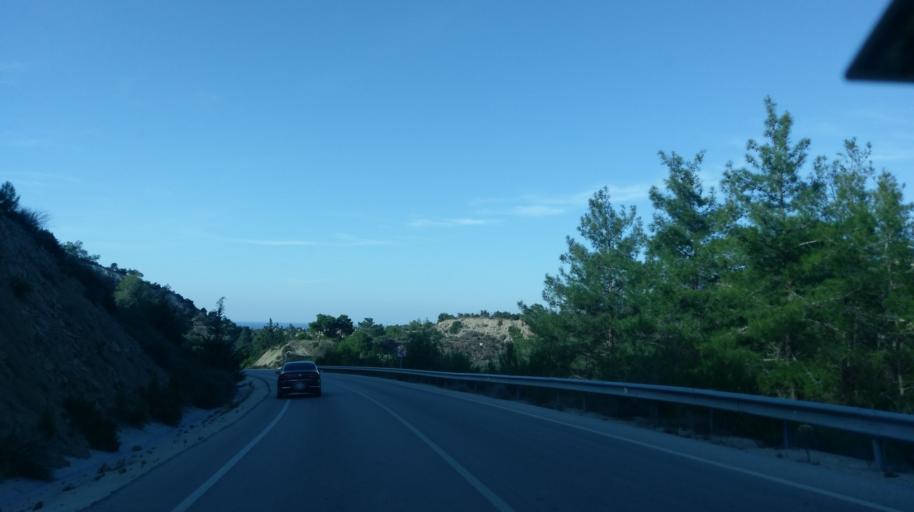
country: CY
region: Ammochostos
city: Lefkonoiko
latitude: 35.3608
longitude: 33.7115
